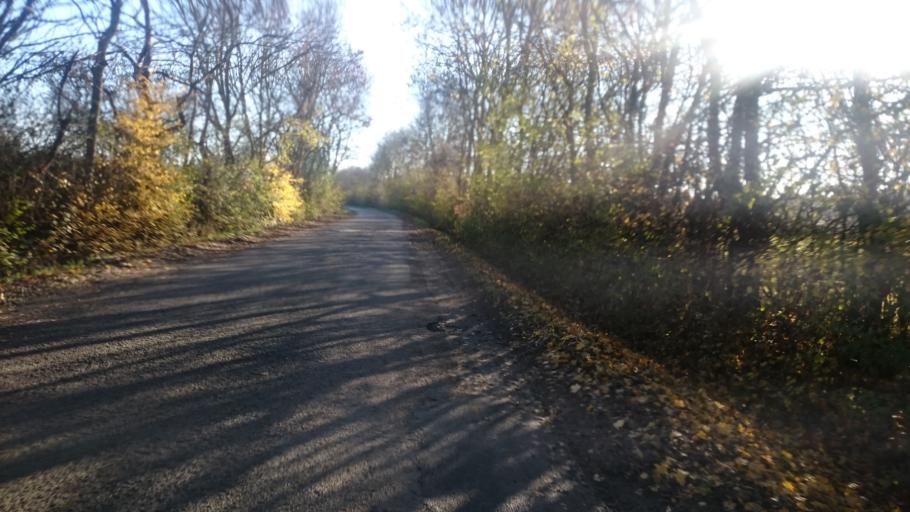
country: FR
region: Bourgogne
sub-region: Departement de Saone-et-Loire
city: Tournus
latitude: 46.5716
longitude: 4.9172
